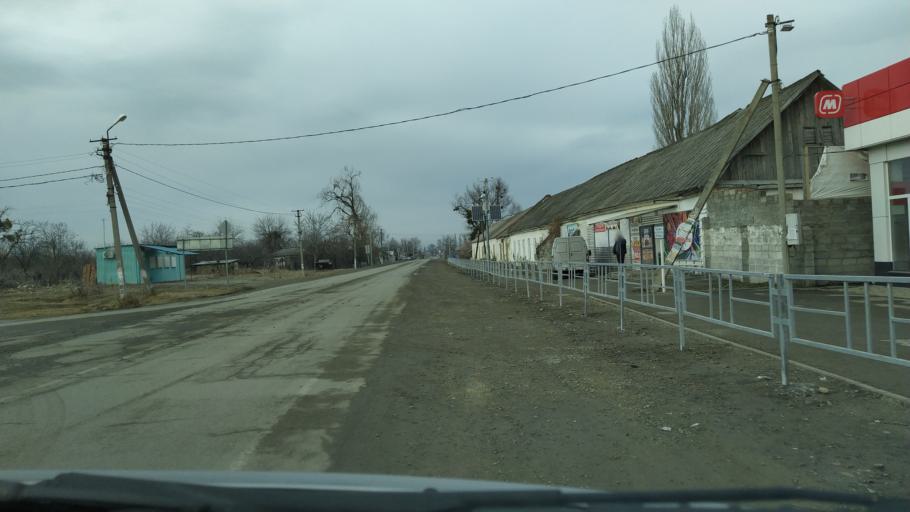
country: RU
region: Krasnodarskiy
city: Udobnaya
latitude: 44.2037
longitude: 41.5568
